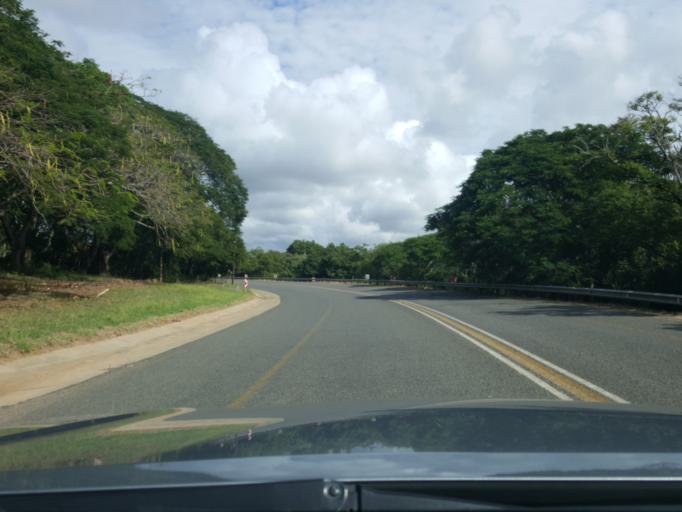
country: ZA
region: Mpumalanga
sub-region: Ehlanzeni District
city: Nelspruit
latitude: -25.4678
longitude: 31.0409
